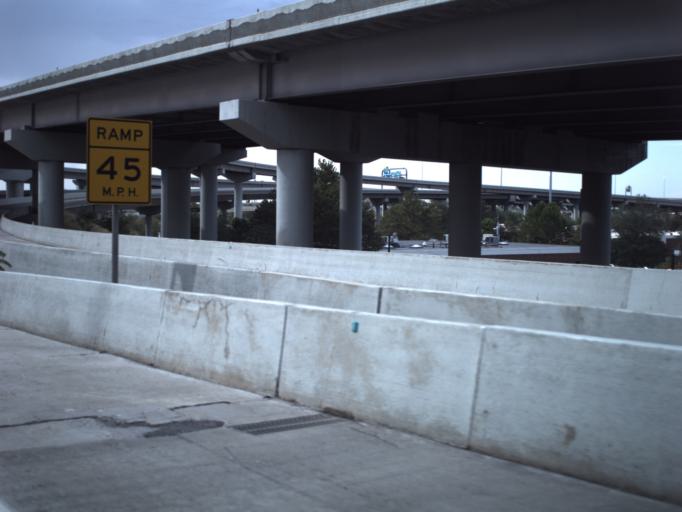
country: US
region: Utah
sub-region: Salt Lake County
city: South Salt Lake
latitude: 40.7183
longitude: -111.9001
